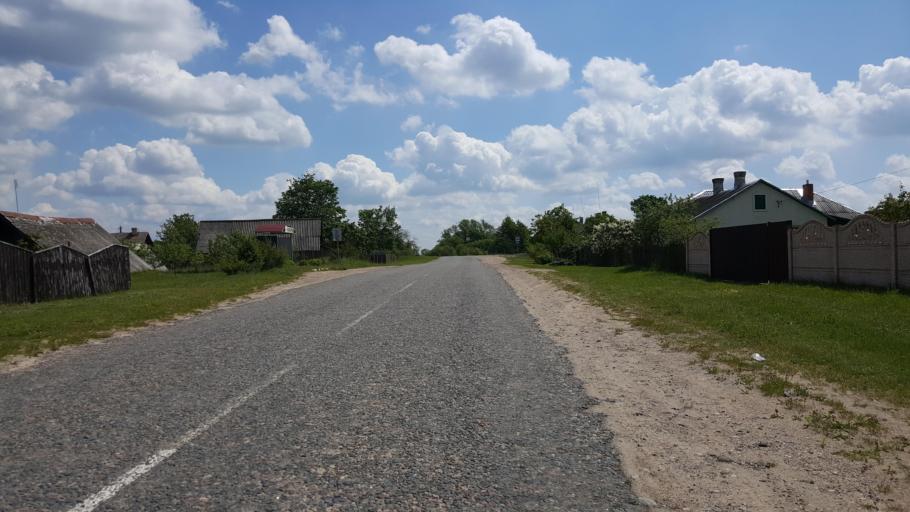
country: BY
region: Brest
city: Kamyanyets
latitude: 52.4156
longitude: 23.9265
